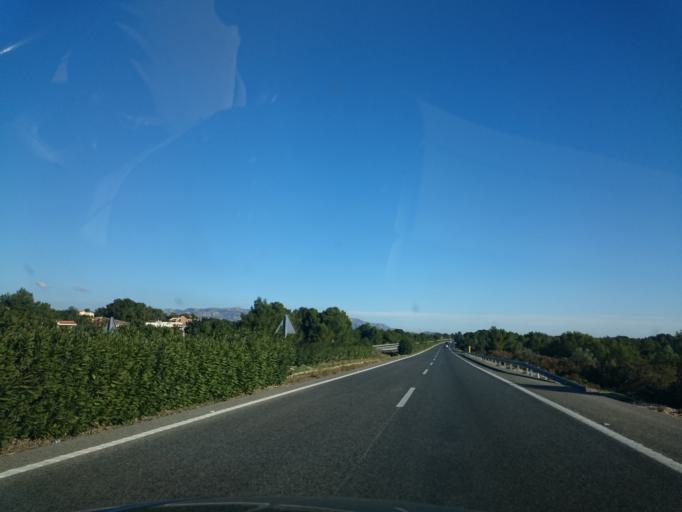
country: ES
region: Catalonia
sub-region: Provincia de Tarragona
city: El Perello
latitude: 40.8556
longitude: 0.7641
